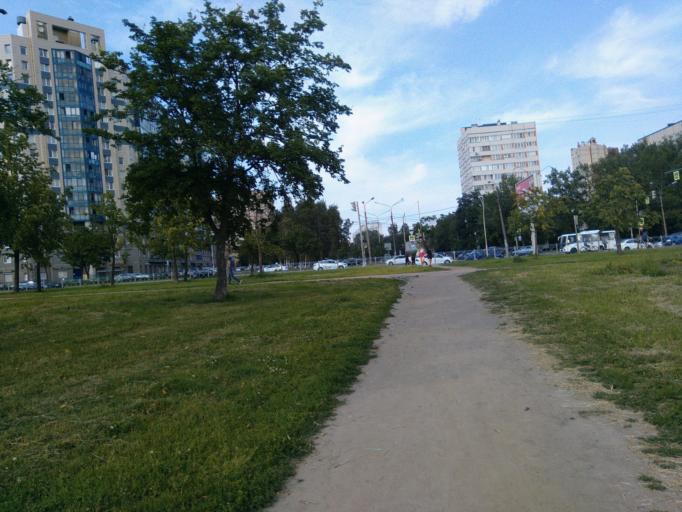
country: RU
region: St.-Petersburg
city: Grazhdanka
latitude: 60.0271
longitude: 30.4026
